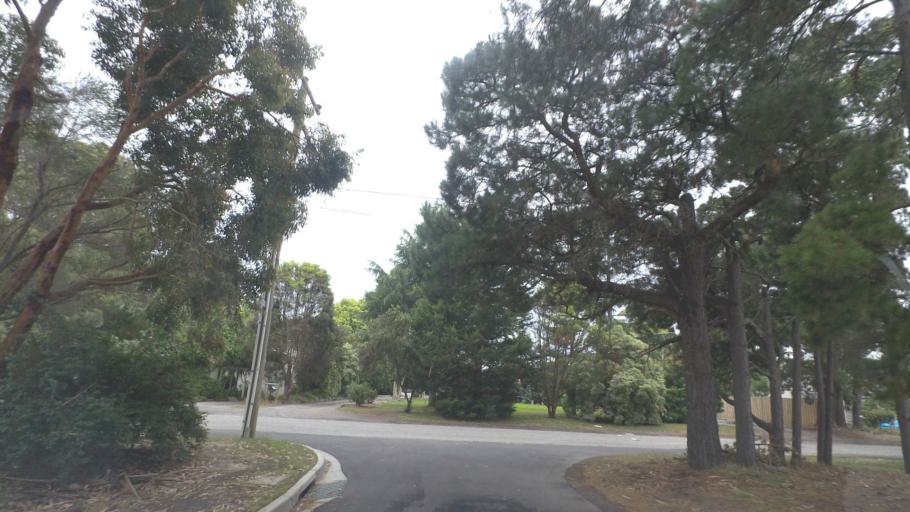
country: AU
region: Victoria
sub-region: Manningham
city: Park Orchards
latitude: -37.7784
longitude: 145.2236
